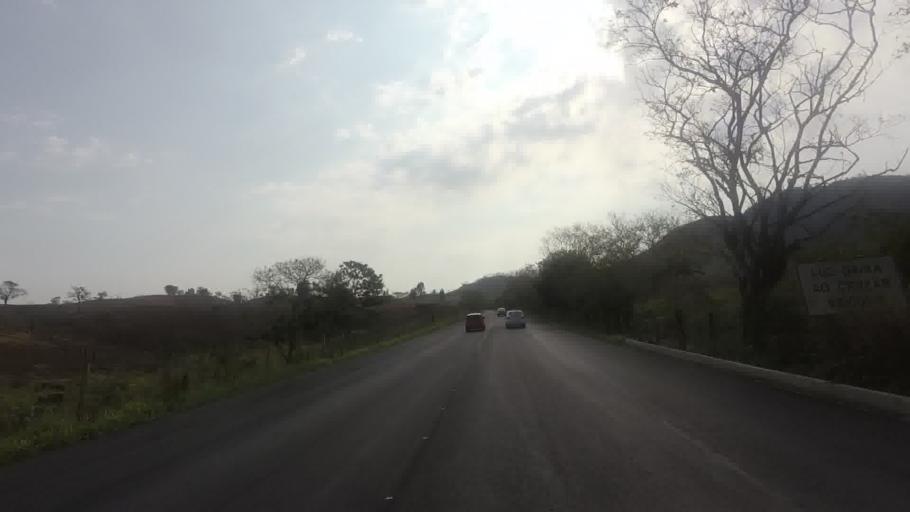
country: BR
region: Rio de Janeiro
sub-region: Bom Jesus Do Itabapoana
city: Bom Jesus do Itabapoana
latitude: -21.1952
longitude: -41.7021
